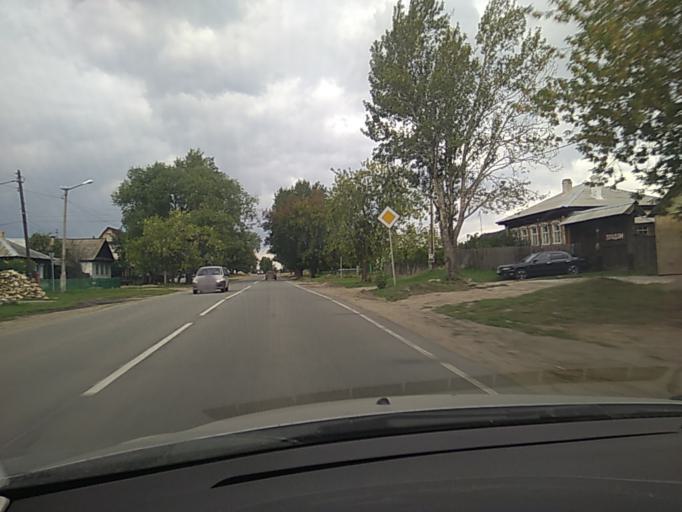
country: RU
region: Chelyabinsk
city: Kyshtym
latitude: 55.7071
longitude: 60.5188
